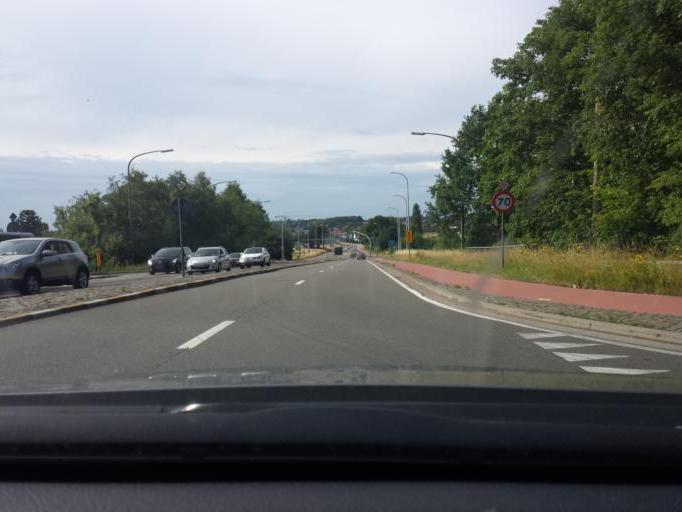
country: BE
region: Flanders
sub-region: Provincie Vlaams-Brabant
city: Wezembeek-Oppem
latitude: 50.8700
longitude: 4.5107
